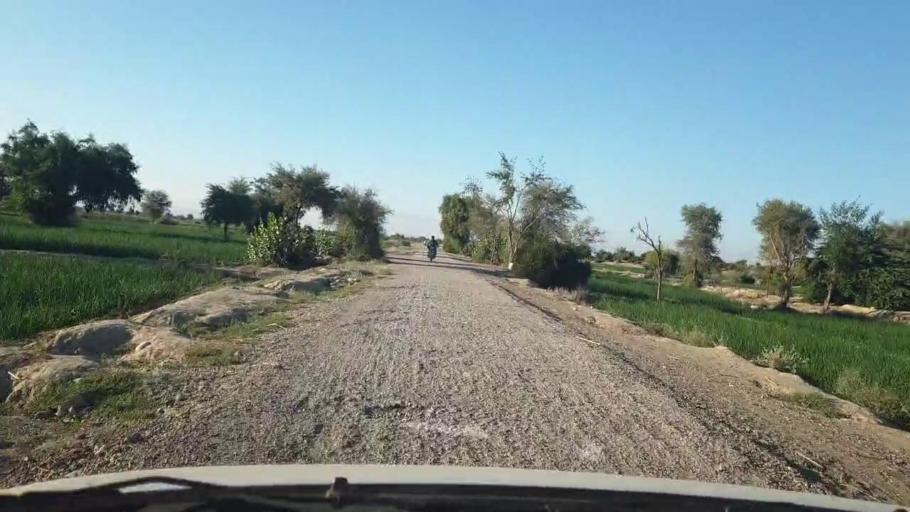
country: PK
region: Sindh
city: Johi
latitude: 26.7617
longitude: 67.4674
